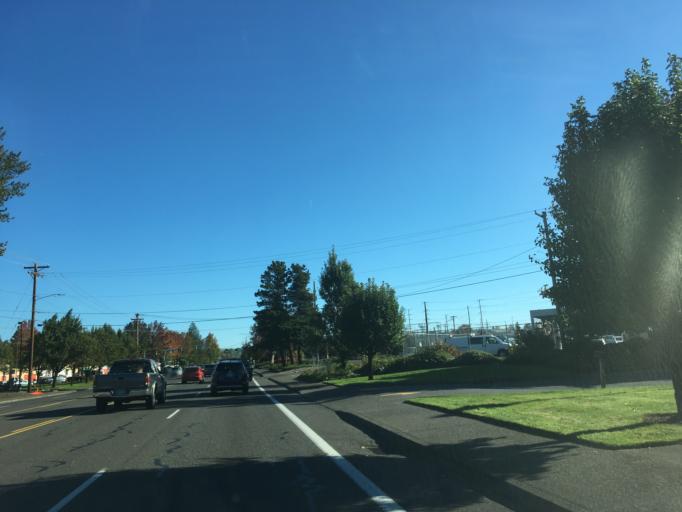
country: US
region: Oregon
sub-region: Multnomah County
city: Gresham
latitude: 45.5031
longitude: -122.4155
